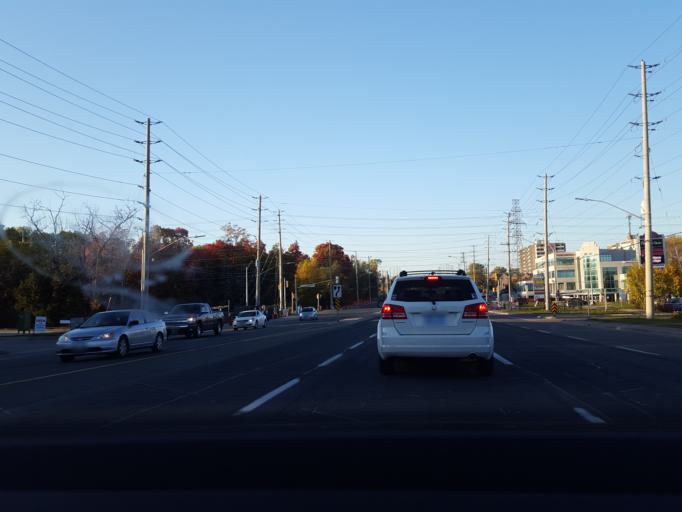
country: CA
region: Ontario
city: Newmarket
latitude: 44.0350
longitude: -79.4757
